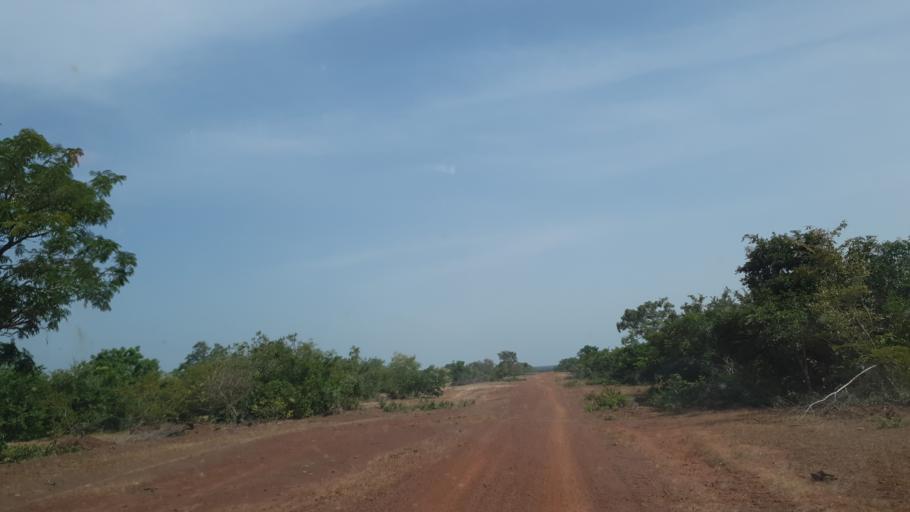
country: ML
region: Koulikoro
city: Dioila
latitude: 12.4611
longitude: -6.1919
